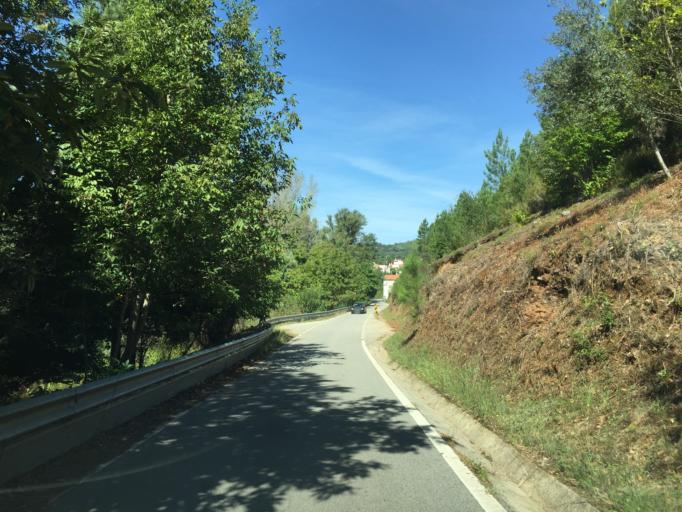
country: PT
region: Portalegre
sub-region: Marvao
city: Marvao
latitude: 39.3789
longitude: -7.3856
